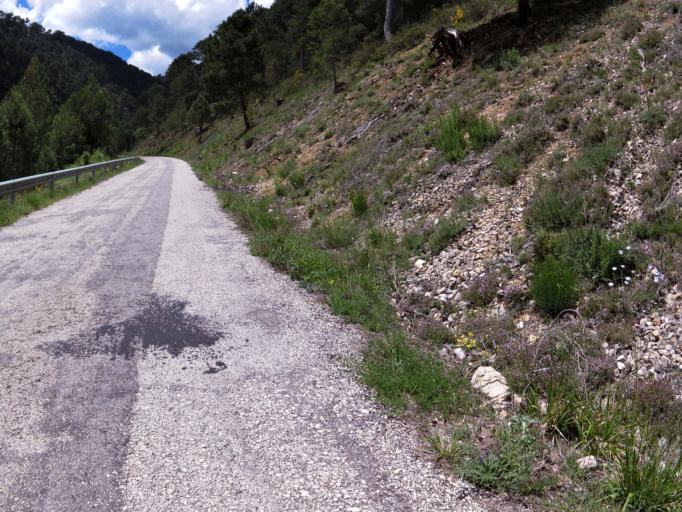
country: ES
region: Castille-La Mancha
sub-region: Provincia de Albacete
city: Paterna del Madera
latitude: 38.5708
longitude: -2.3587
